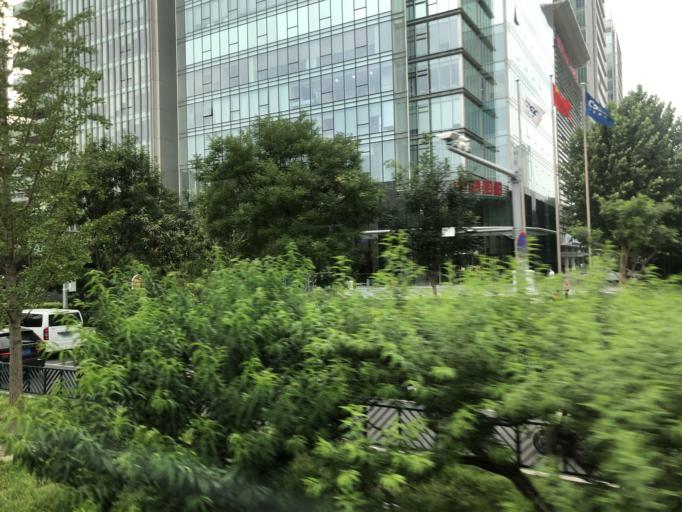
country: CN
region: Beijing
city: Jinrongjie
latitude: 39.9311
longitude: 116.3191
